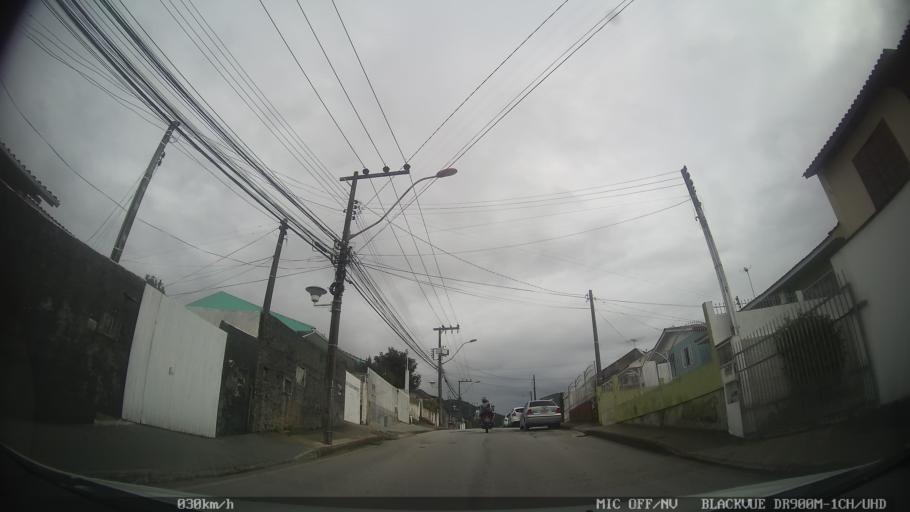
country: BR
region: Santa Catarina
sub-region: Sao Jose
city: Campinas
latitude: -27.5700
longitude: -48.6274
